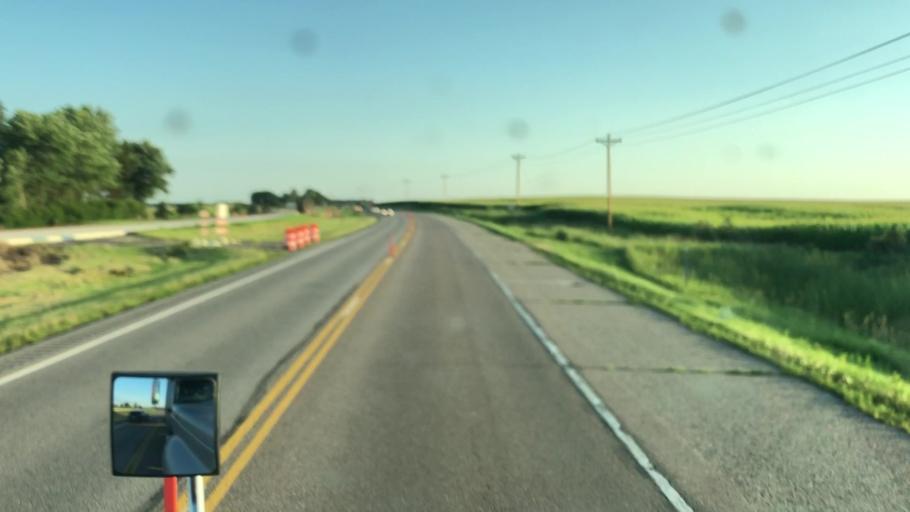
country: US
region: Minnesota
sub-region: Scott County
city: Belle Plaine
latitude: 44.5637
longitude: -93.8491
